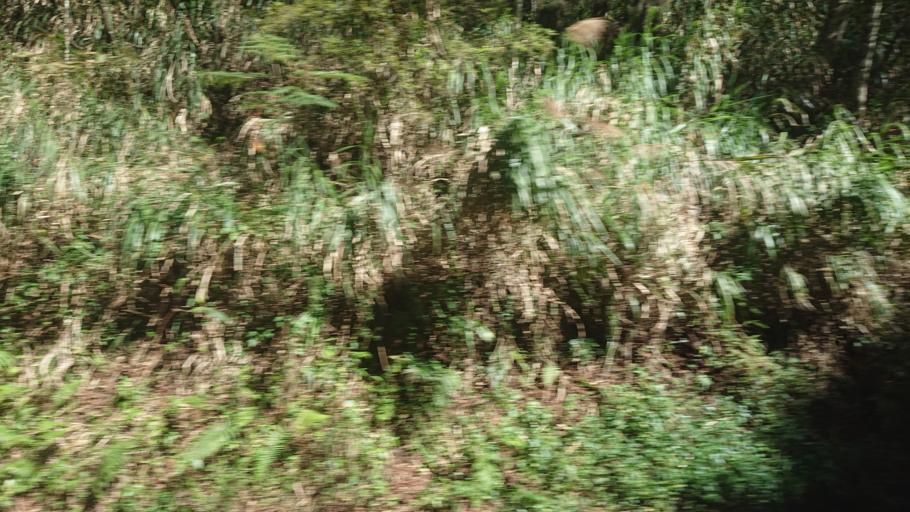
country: TW
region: Taiwan
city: Lugu
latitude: 23.4970
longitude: 120.7865
